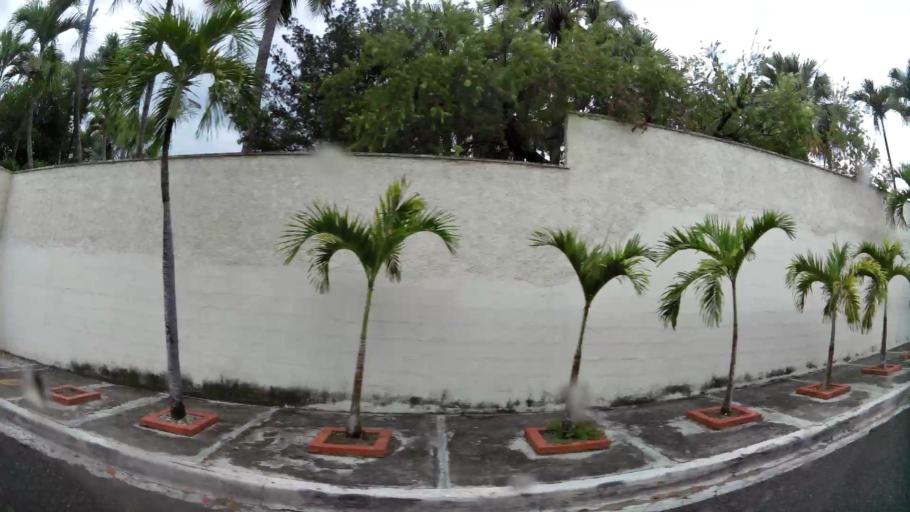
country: DO
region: Nacional
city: La Agustina
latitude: 18.4993
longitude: -69.9381
